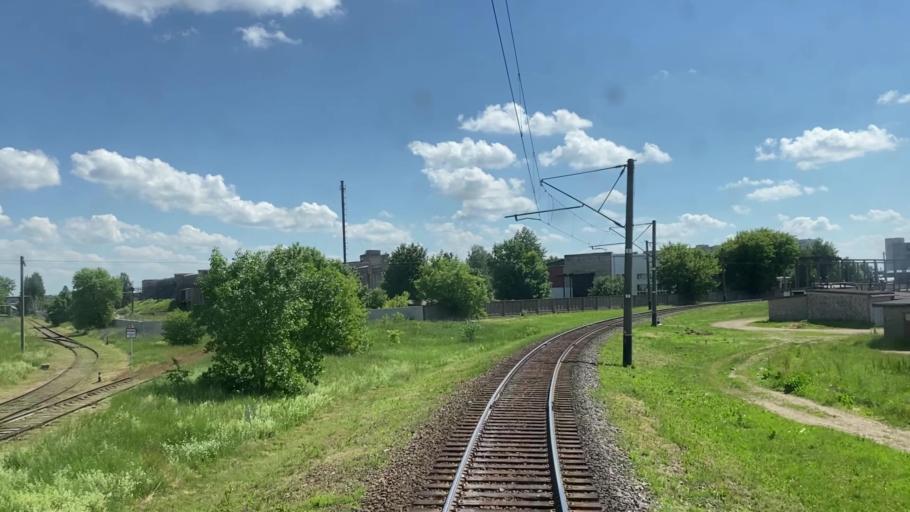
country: BY
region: Brest
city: Baranovichi
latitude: 53.1460
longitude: 26.0291
